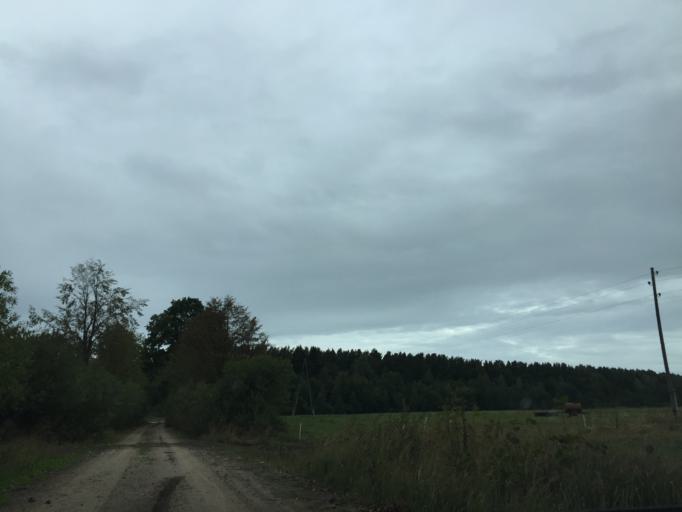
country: LV
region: Salacgrivas
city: Salacgriva
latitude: 57.7034
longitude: 24.3602
